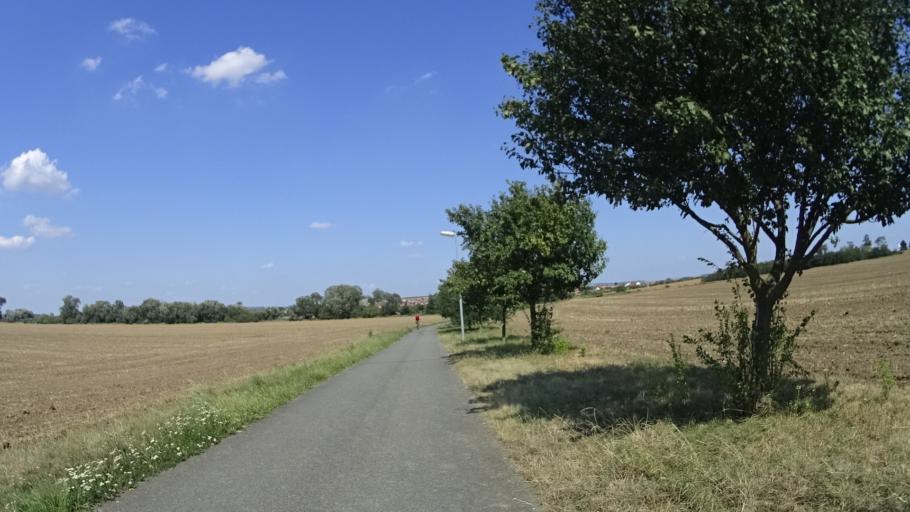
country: CZ
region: Zlin
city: Uhersky Ostroh
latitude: 48.9928
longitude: 17.4131
